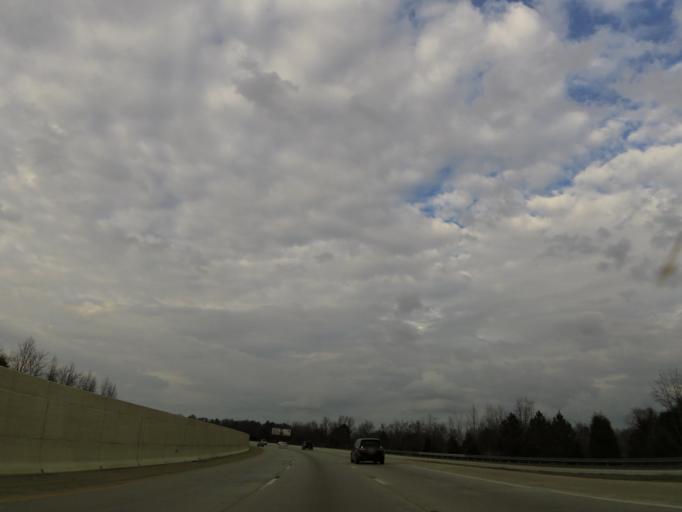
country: US
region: South Carolina
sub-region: Greenville County
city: Mauldin
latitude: 34.7700
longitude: -82.2734
